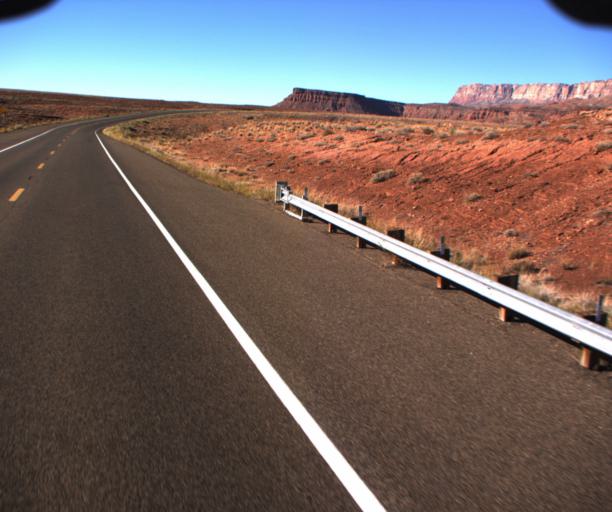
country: US
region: Arizona
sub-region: Coconino County
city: Page
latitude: 36.7827
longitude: -111.6881
